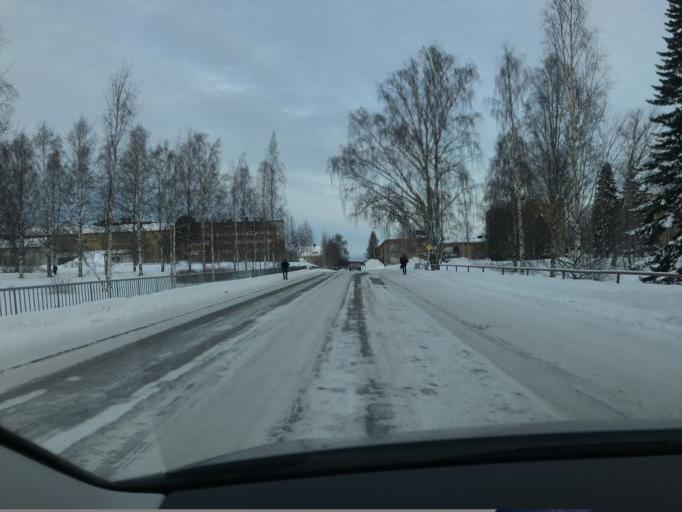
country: SE
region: Norrbotten
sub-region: Lulea Kommun
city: Lulea
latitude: 65.5818
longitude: 22.1370
